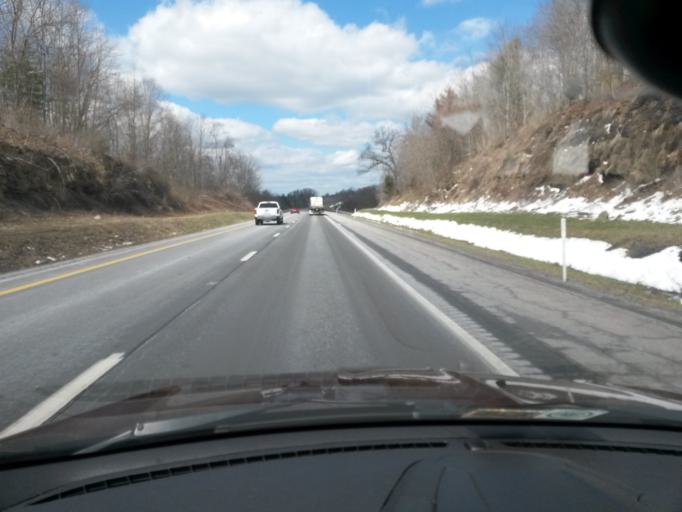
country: US
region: West Virginia
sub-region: Raleigh County
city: Shady Spring
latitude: 37.6444
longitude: -81.1089
